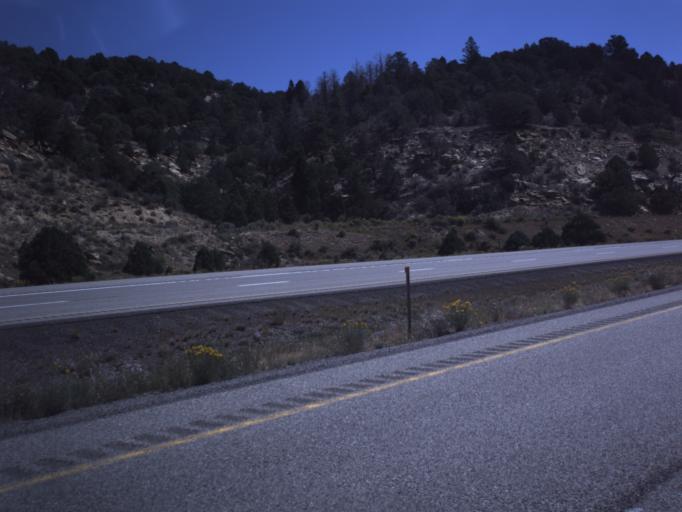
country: US
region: Utah
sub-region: Sevier County
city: Salina
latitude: 38.7951
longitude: -111.5083
